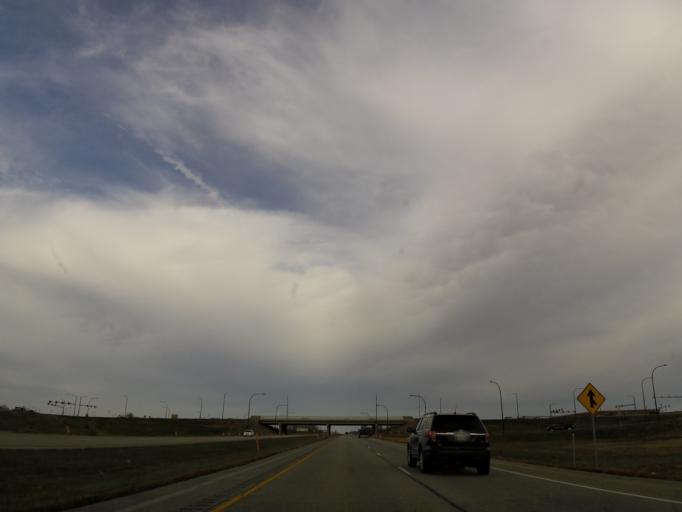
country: US
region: Iowa
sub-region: Scott County
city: Bettendorf
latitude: 41.5722
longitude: -90.5221
